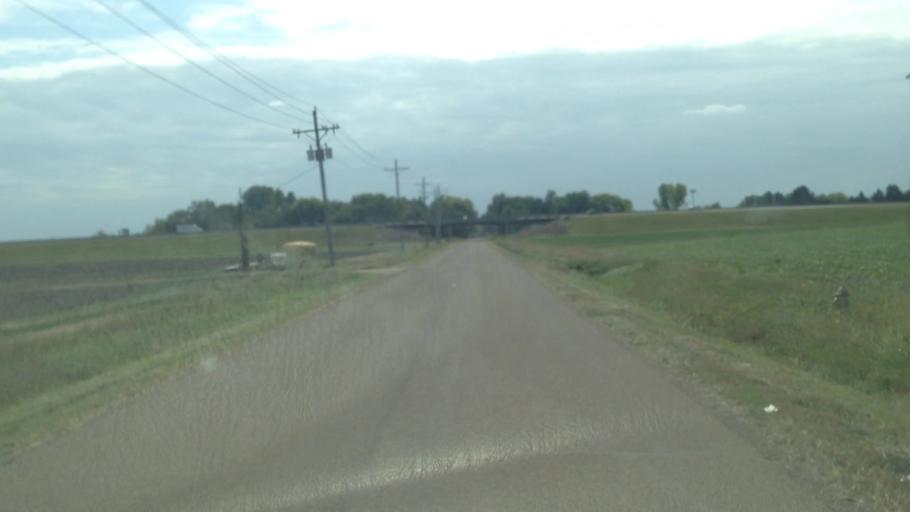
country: US
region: Kansas
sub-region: Douglas County
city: Lawrence
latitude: 38.9966
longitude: -95.2241
